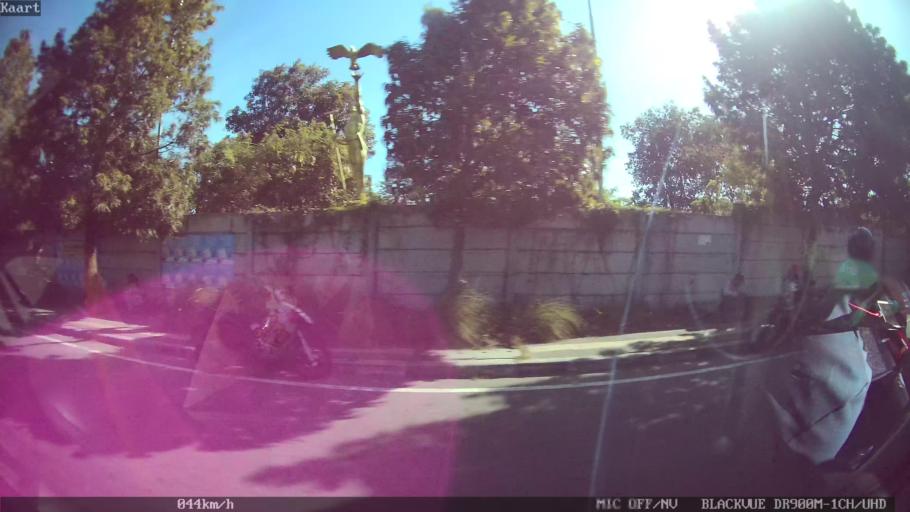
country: ID
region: Bali
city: Banjar Kertasari
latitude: -8.6265
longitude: 115.1947
